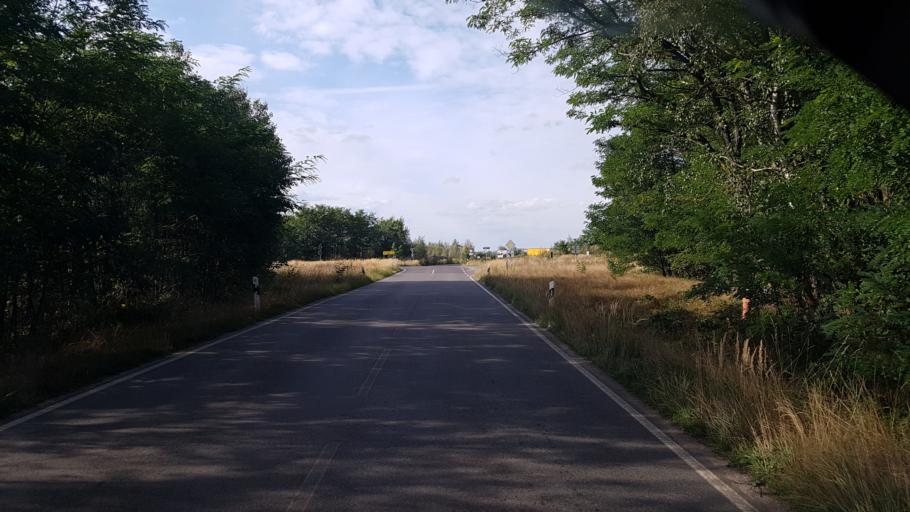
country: DE
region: Brandenburg
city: Welzow
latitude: 51.5501
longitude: 14.2273
